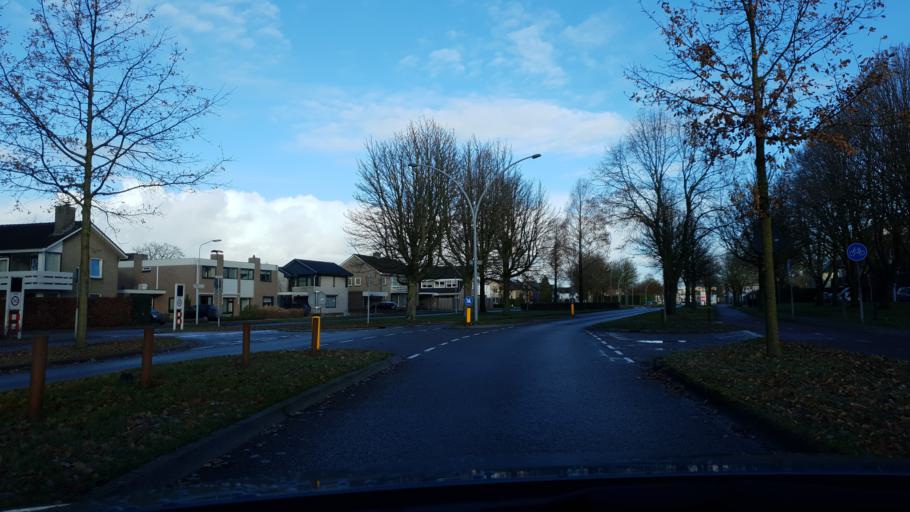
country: NL
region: Gelderland
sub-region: Gemeente Wijchen
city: Wijchen
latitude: 51.8056
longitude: 5.7199
